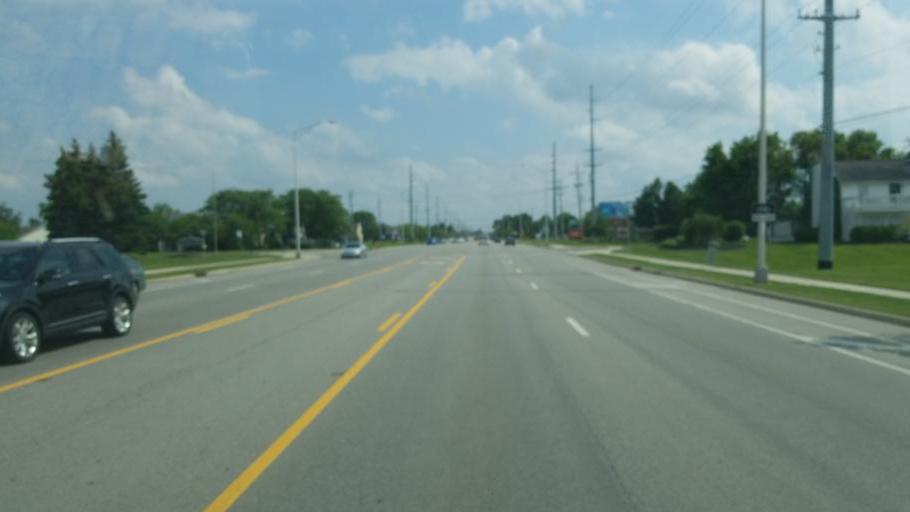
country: US
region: Ohio
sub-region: Franklin County
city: Hilliard
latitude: 39.9978
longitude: -83.1530
